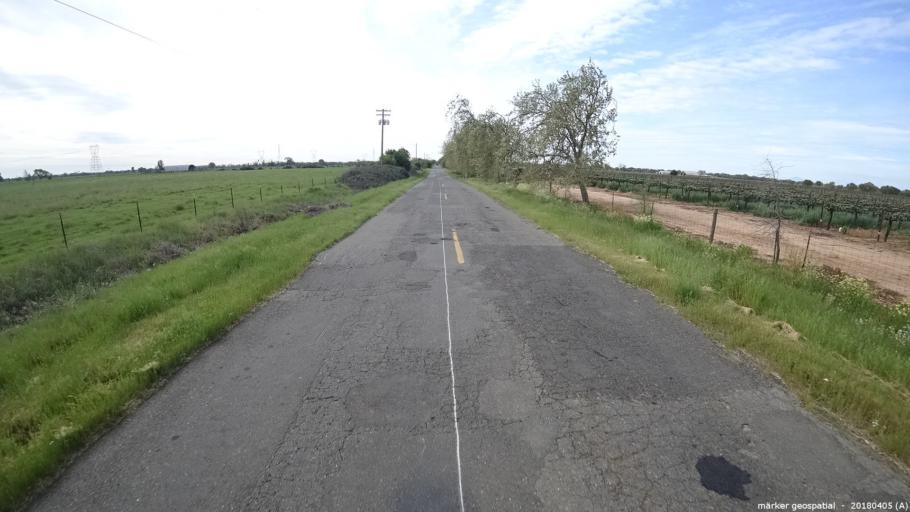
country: US
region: California
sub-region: San Joaquin County
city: Thornton
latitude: 38.2524
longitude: -121.3694
